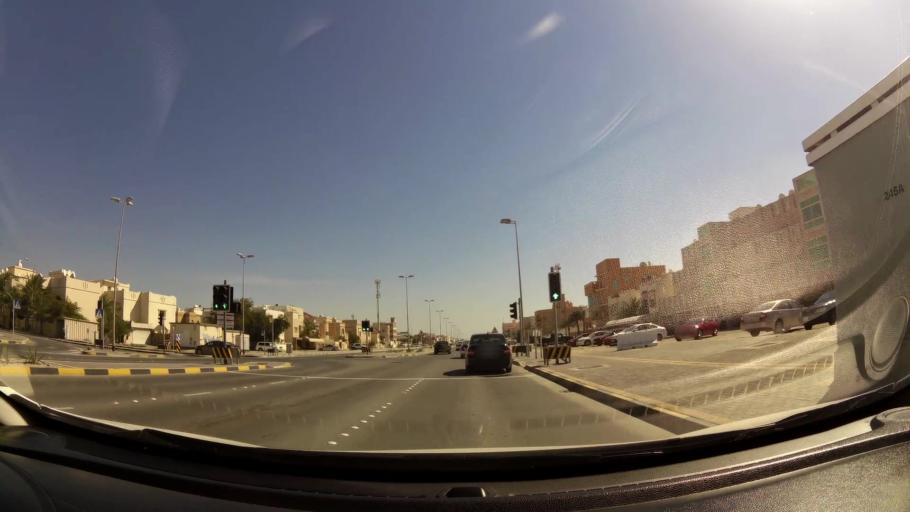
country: BH
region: Muharraq
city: Al Hadd
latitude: 26.2512
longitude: 50.6397
